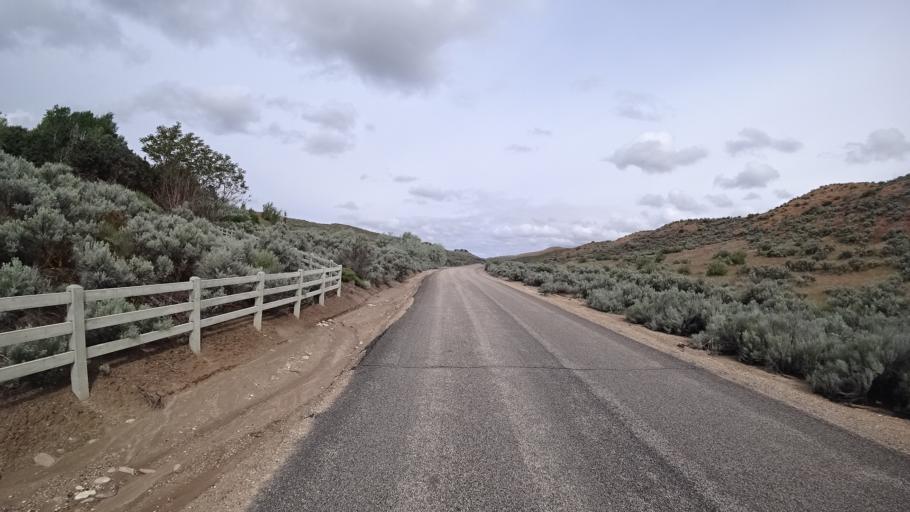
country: US
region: Idaho
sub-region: Ada County
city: Eagle
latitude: 43.7500
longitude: -116.3586
